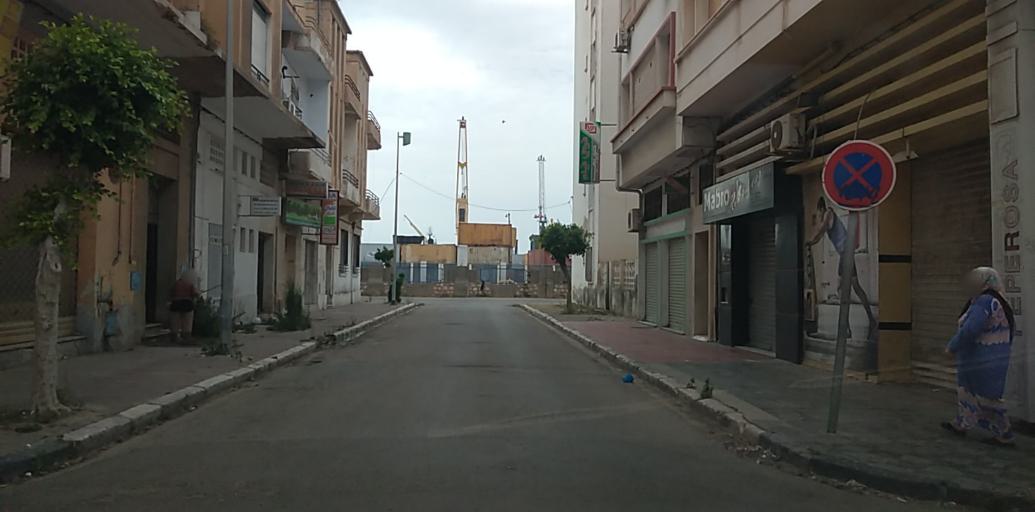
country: TN
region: Safaqis
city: Sfax
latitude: 34.7305
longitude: 10.7655
